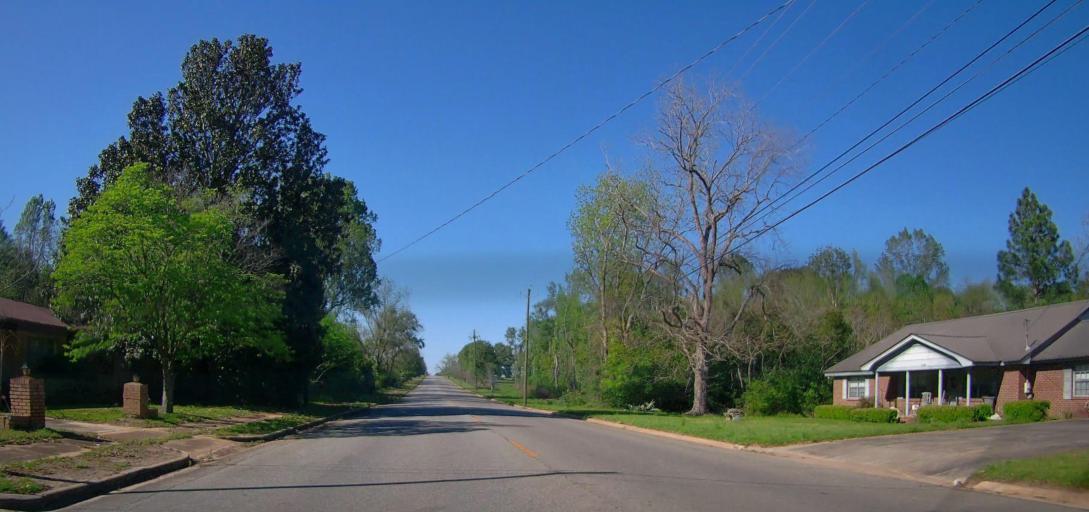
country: US
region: Georgia
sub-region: Wilcox County
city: Rochelle
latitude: 31.9544
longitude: -83.4563
